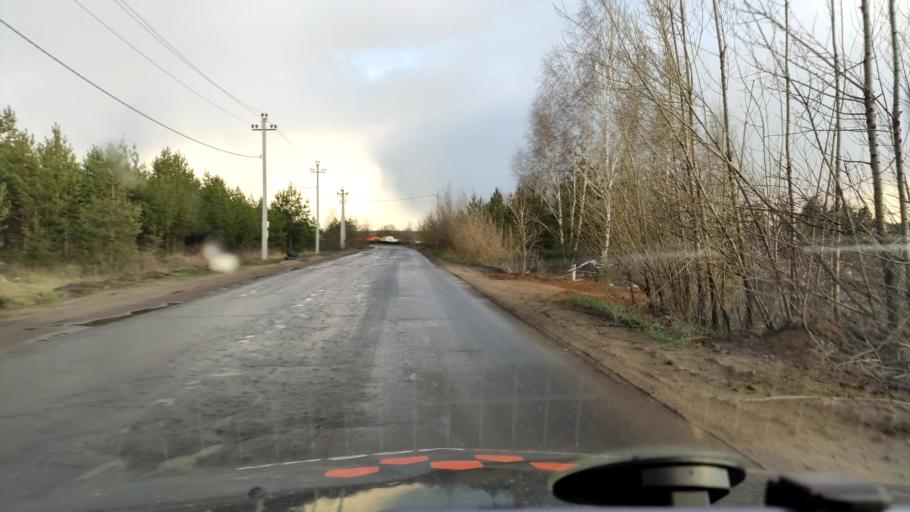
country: RU
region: Voronezj
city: Podgornoye
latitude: 51.8299
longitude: 39.2069
